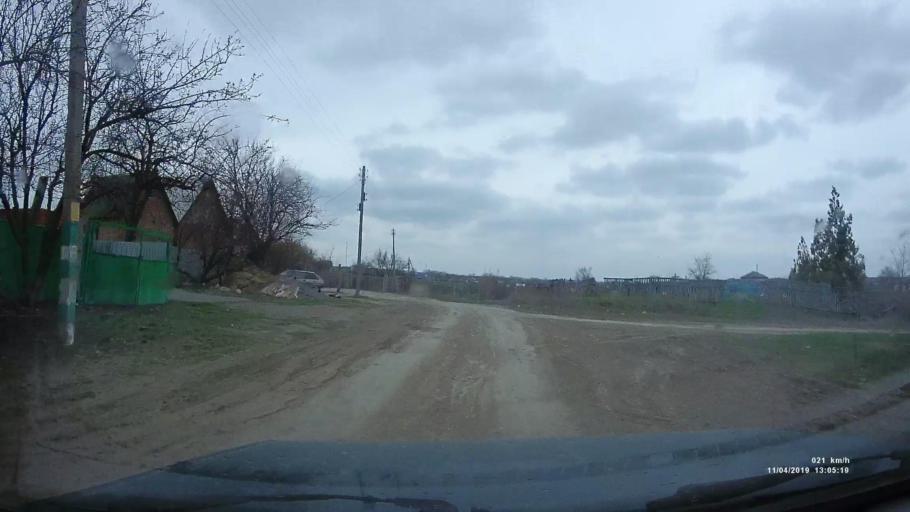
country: RU
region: Rostov
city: Staraya Stanitsa
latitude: 48.2866
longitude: 40.3431
